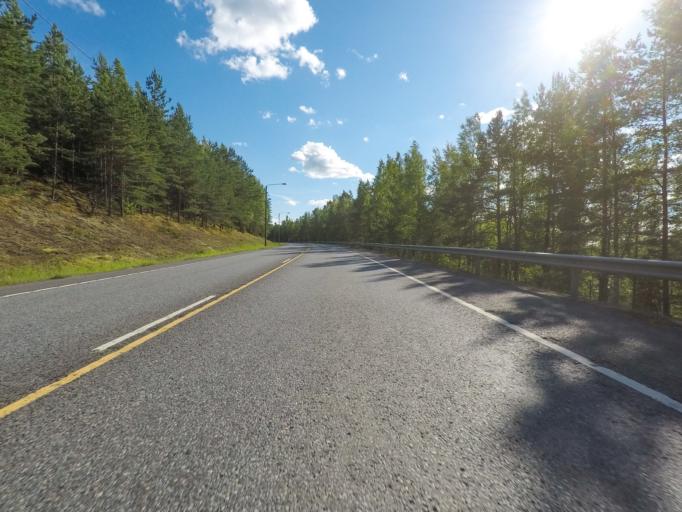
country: FI
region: Uusimaa
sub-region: Helsinki
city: Vihti
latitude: 60.3369
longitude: 24.2921
